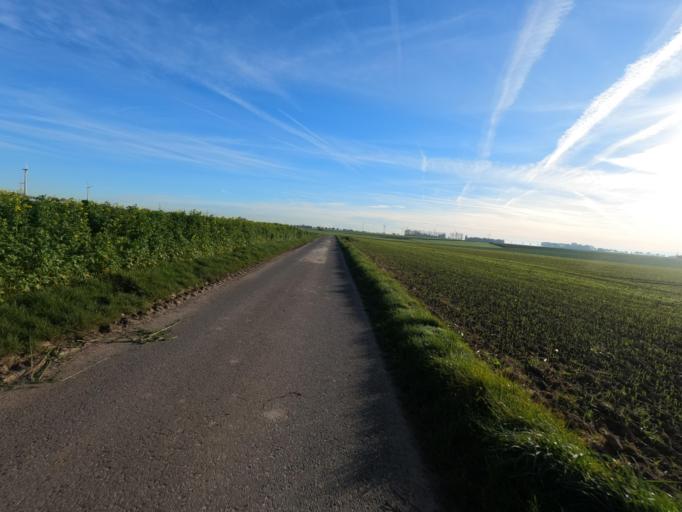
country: DE
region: North Rhine-Westphalia
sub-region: Regierungsbezirk Koln
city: Titz
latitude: 51.0356
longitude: 6.3676
